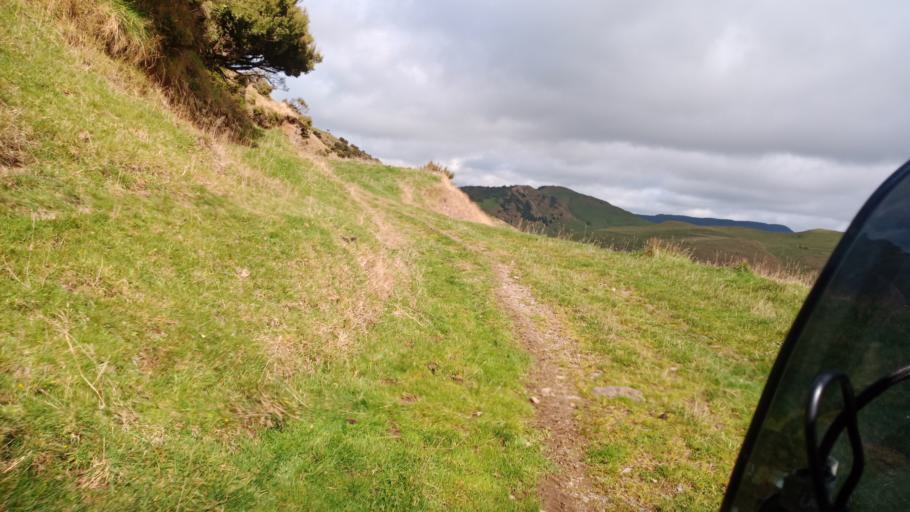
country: NZ
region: Gisborne
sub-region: Gisborne District
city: Gisborne
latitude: -38.4721
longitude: 177.5361
